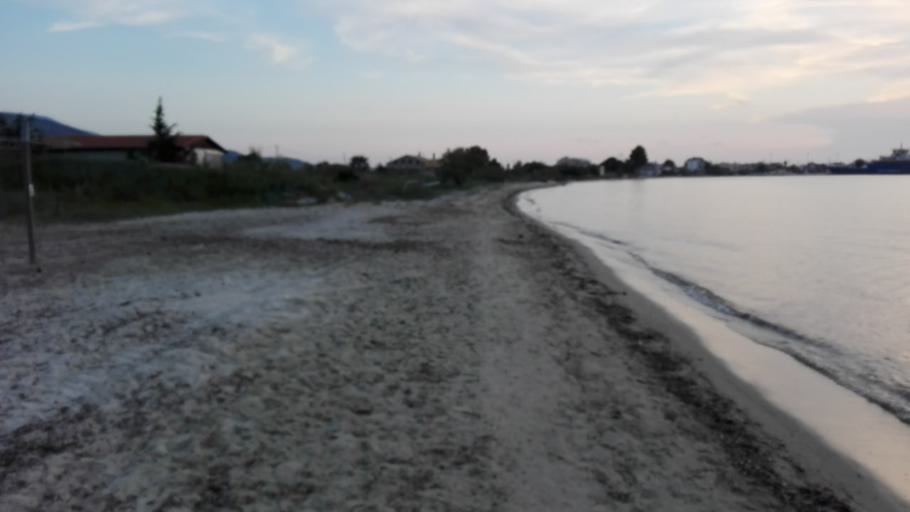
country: GR
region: East Macedonia and Thrace
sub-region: Nomos Kavalas
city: Prinos
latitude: 40.7605
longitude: 24.5848
